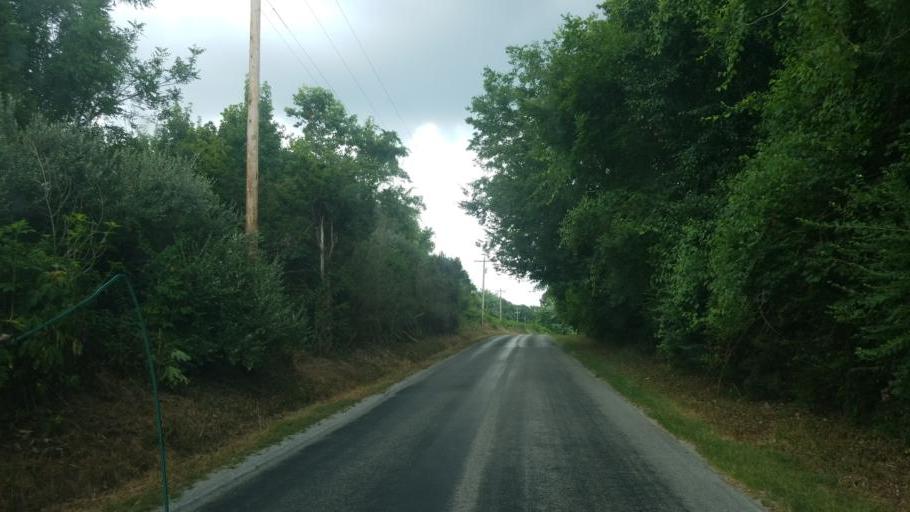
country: US
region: Illinois
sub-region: Jackson County
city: Murphysboro
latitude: 37.7070
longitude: -89.3316
